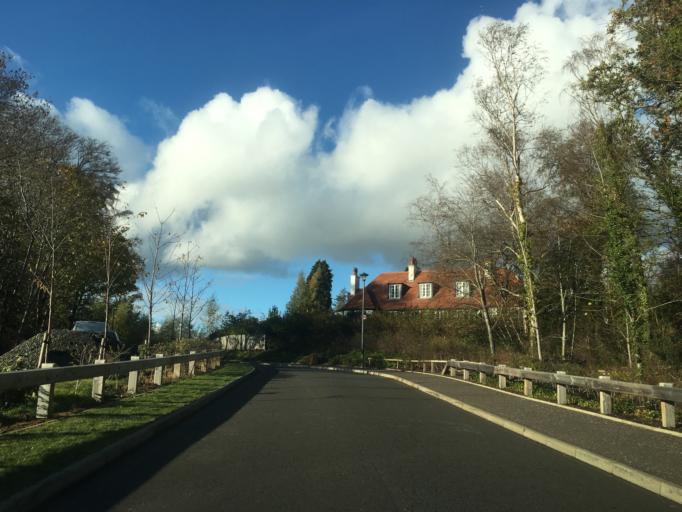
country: GB
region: Scotland
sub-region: Edinburgh
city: Colinton
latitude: 55.9025
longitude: -3.2497
